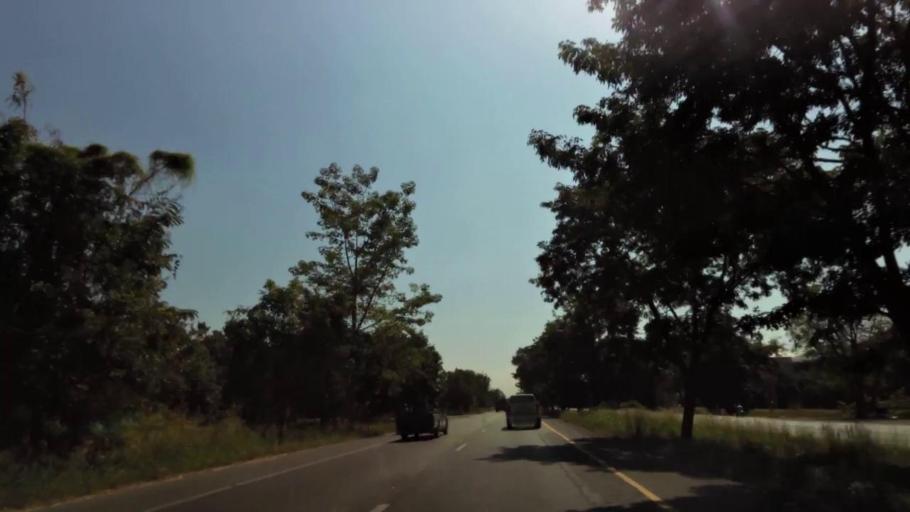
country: TH
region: Nakhon Sawan
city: Kao Liao
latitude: 15.8517
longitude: 100.1172
